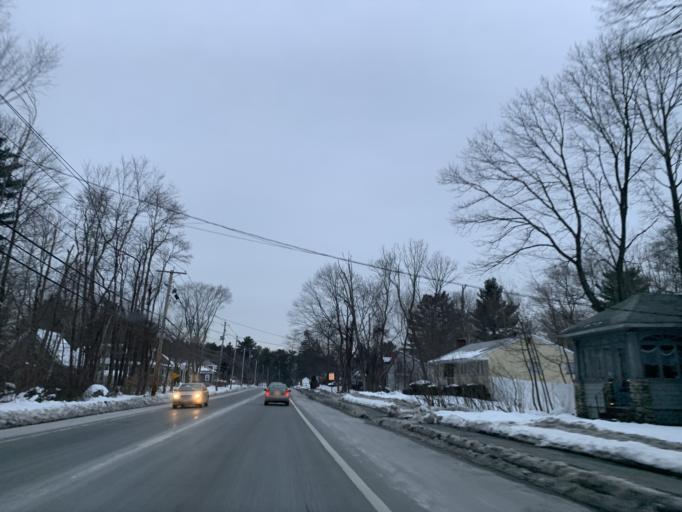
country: US
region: Massachusetts
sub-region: Norfolk County
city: Stoughton
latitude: 42.1139
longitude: -71.0782
